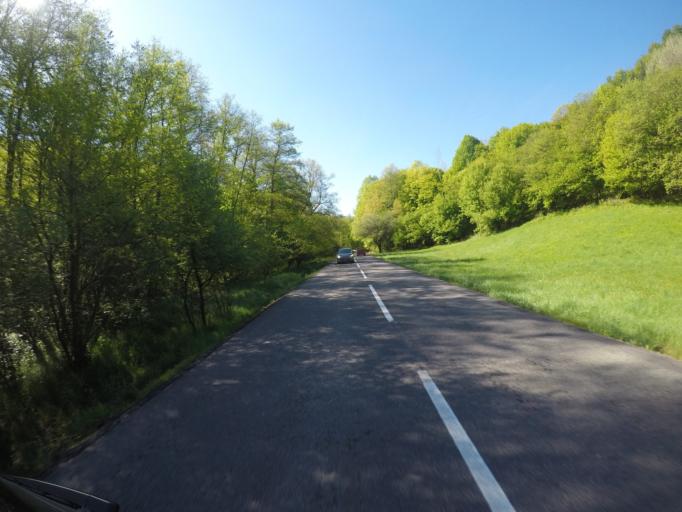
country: SK
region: Banskobystricky
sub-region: Okres Banska Bystrica
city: Banska Stiavnica
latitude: 48.5333
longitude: 19.0059
